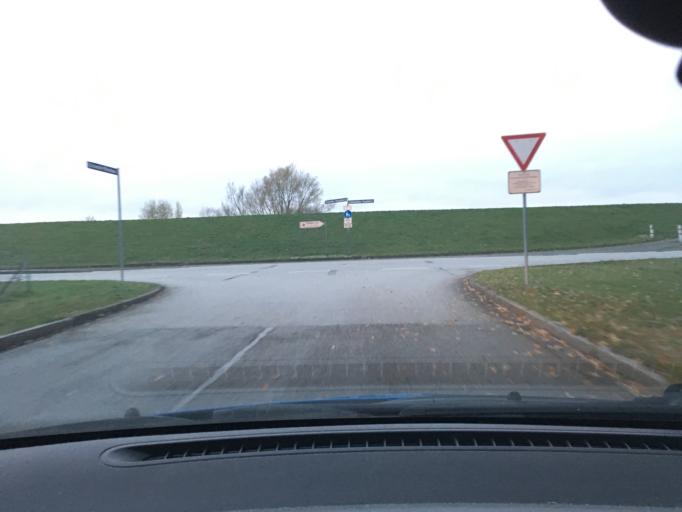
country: DE
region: Lower Saxony
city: Winsen
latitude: 53.4024
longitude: 10.2051
